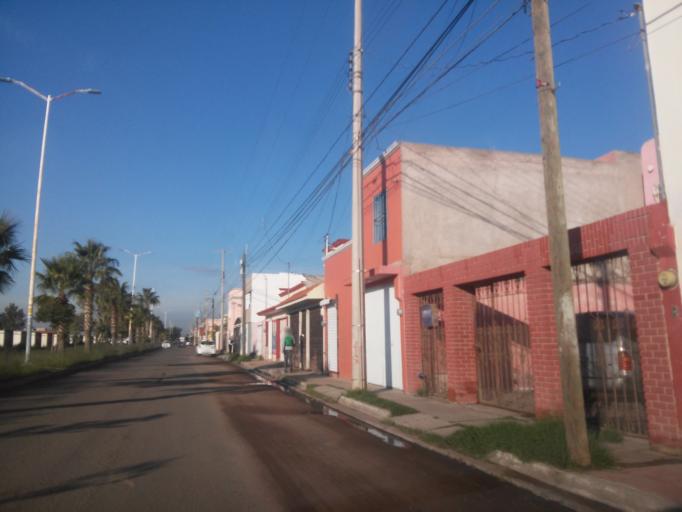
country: MX
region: Durango
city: Victoria de Durango
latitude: 24.0490
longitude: -104.6127
